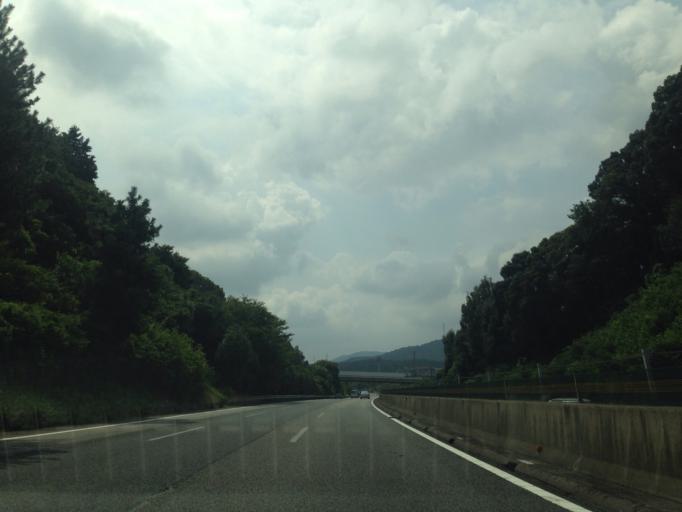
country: JP
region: Aichi
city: Gamagori
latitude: 34.9001
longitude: 137.2560
